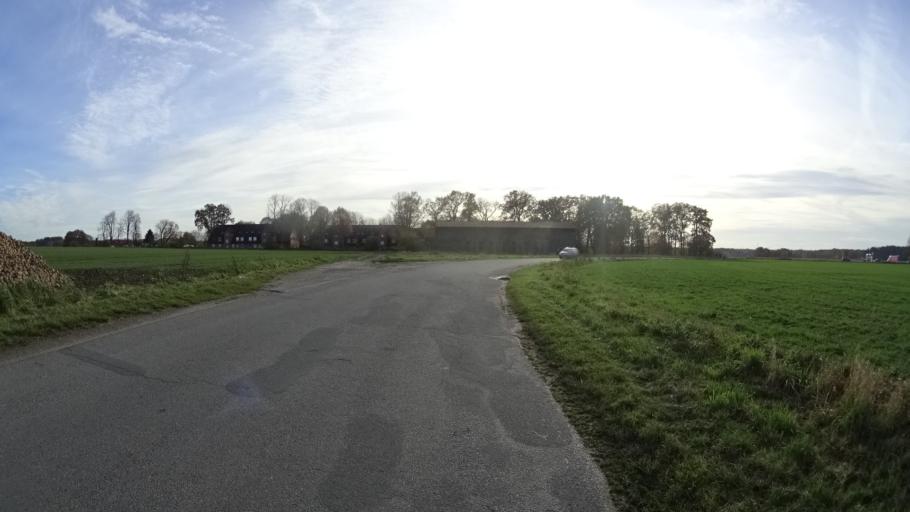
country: DE
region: Lower Saxony
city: Wendisch Evern
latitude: 53.2262
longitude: 10.4587
